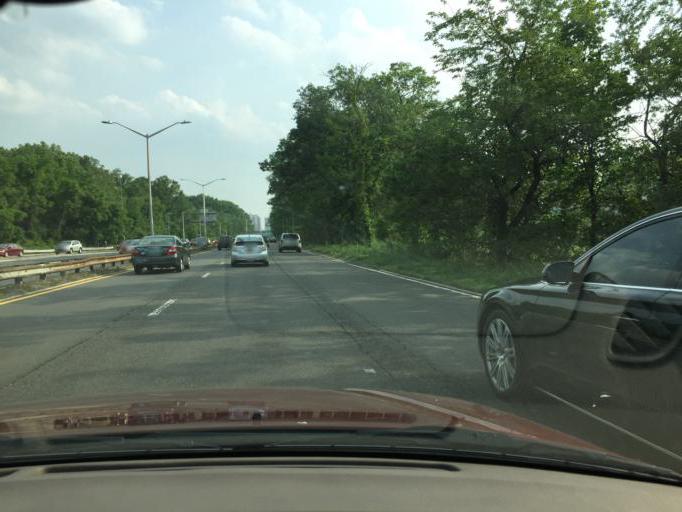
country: US
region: New York
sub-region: Westchester County
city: Pelham Manor
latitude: 40.8846
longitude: -73.8158
